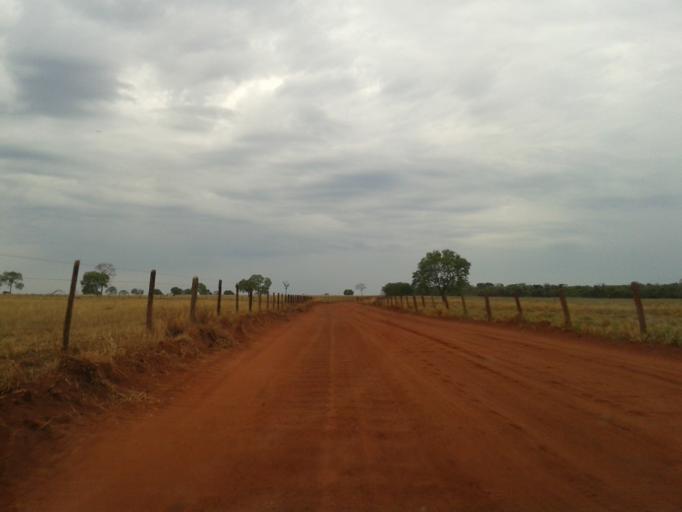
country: BR
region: Minas Gerais
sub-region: Ituiutaba
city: Ituiutaba
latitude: -18.9371
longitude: -49.7341
